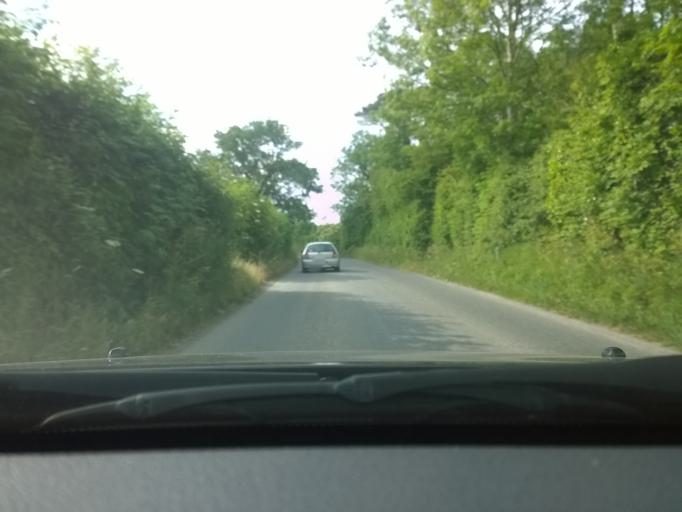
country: IE
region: Leinster
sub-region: Kildare
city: Rathangan
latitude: 53.2033
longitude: -6.9558
